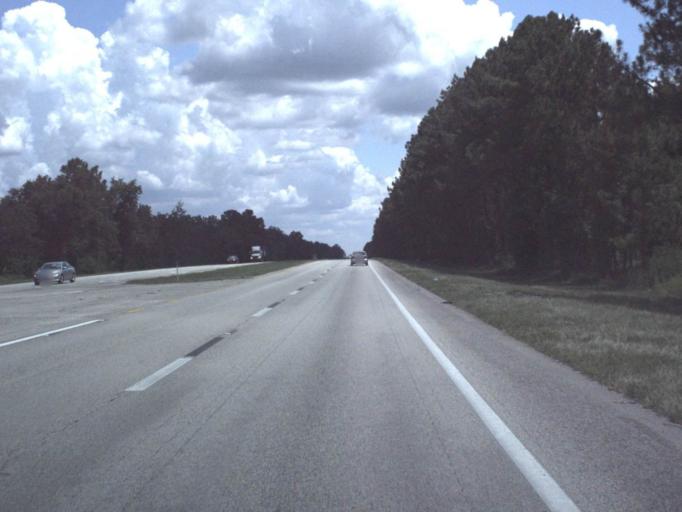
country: US
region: Florida
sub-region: Alachua County
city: Hawthorne
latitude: 29.6836
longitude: -82.1255
